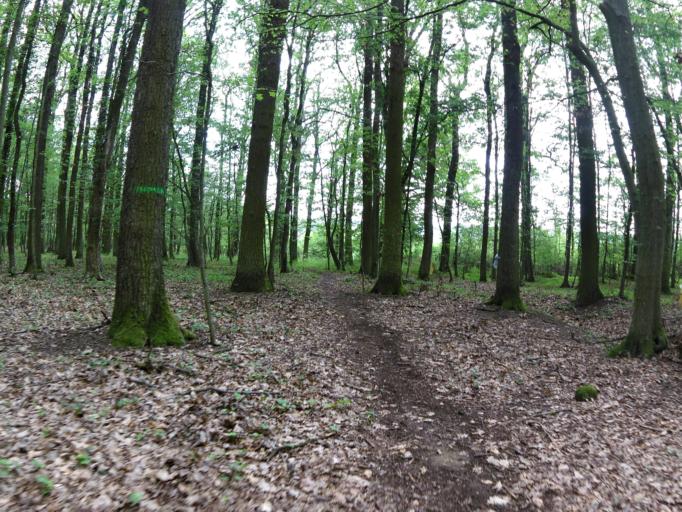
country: DE
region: Bavaria
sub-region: Regierungsbezirk Unterfranken
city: Sommerhausen
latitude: 49.7126
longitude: 10.0305
